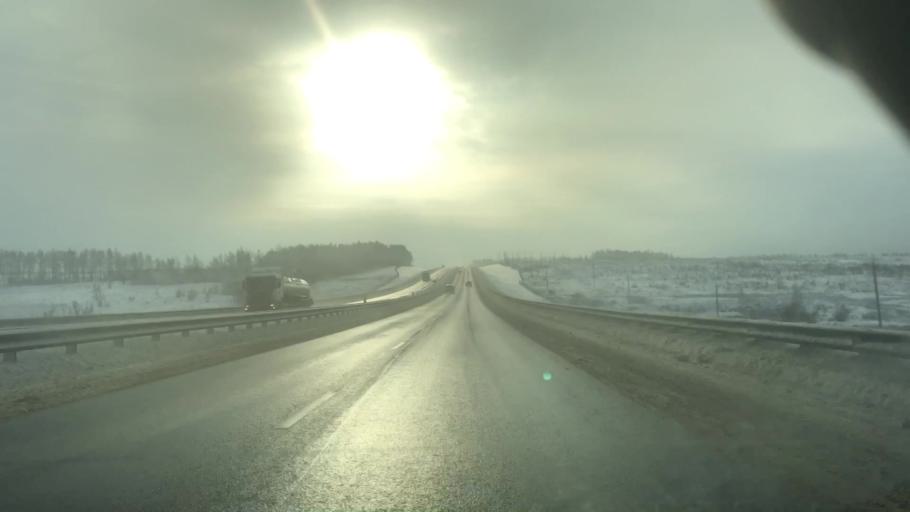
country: RU
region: Tula
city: Venev
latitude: 54.3205
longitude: 38.1544
